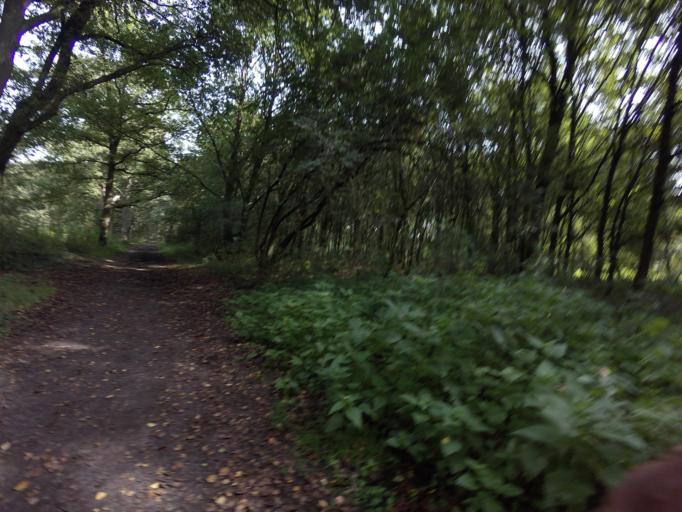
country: NL
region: Overijssel
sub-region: Gemeente Enschede
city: Enschede
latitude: 52.1896
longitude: 6.9490
